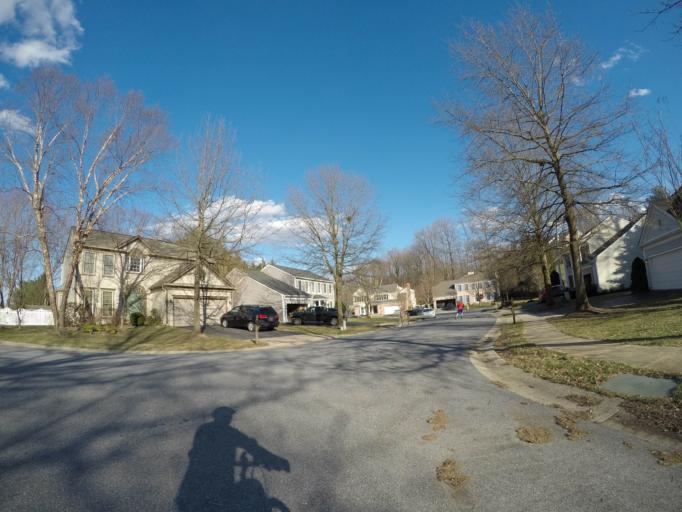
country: US
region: Maryland
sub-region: Howard County
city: Ellicott City
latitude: 39.2597
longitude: -76.8035
